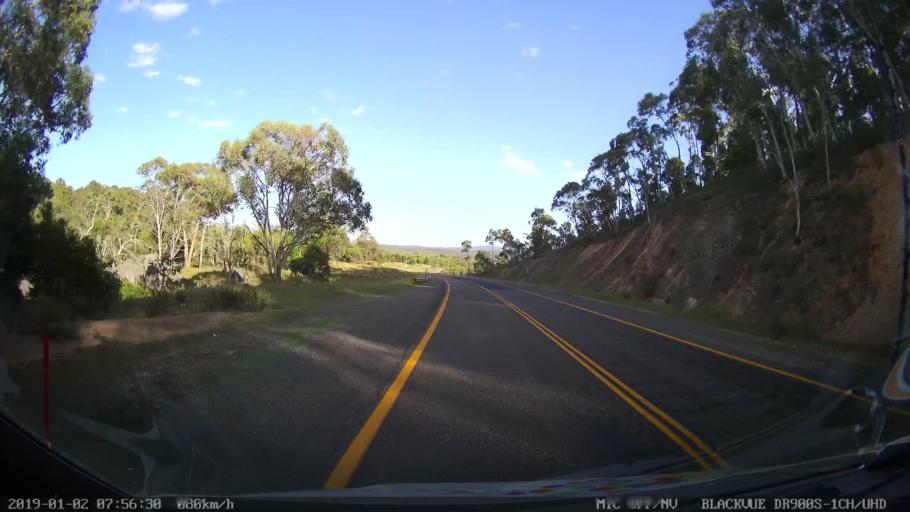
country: AU
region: New South Wales
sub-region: Tumut Shire
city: Tumut
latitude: -35.6701
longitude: 148.4848
